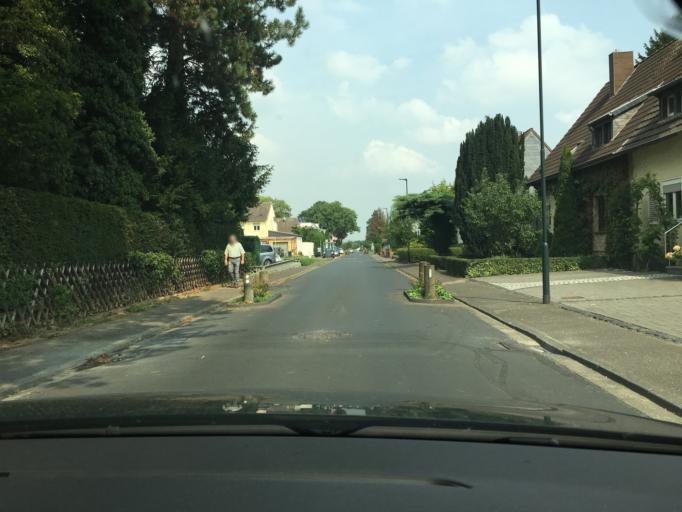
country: DE
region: North Rhine-Westphalia
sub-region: Regierungsbezirk Koln
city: Merzenich
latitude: 50.8627
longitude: 6.5816
